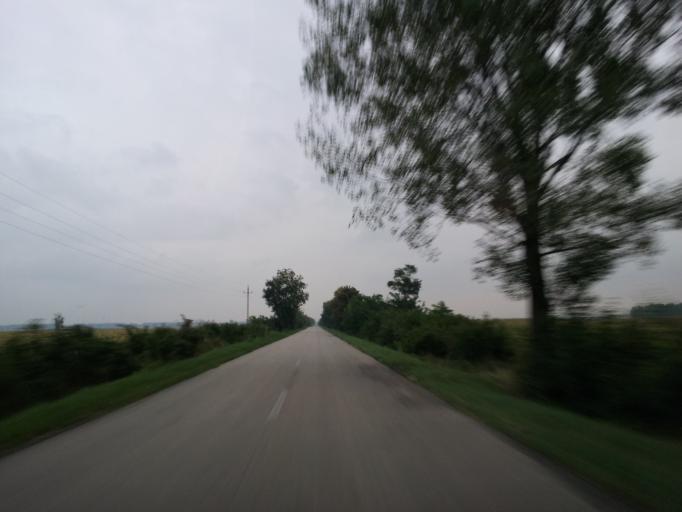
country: HU
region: Tolna
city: Fadd
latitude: 46.4866
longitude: 18.8535
